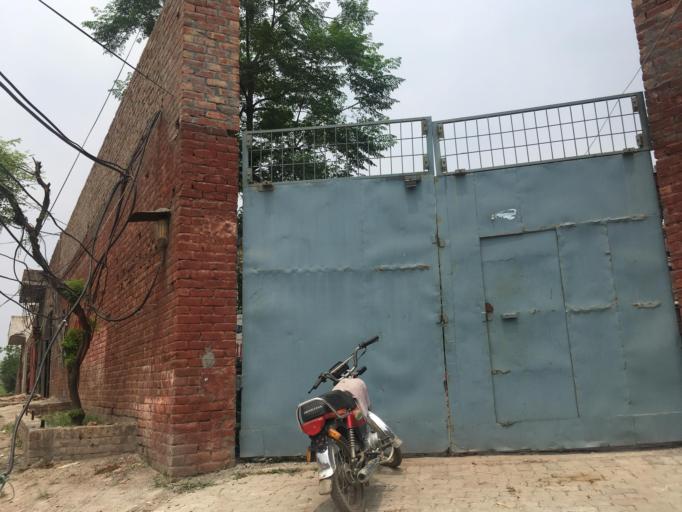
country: PK
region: Punjab
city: Lahore
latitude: 31.6126
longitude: 74.3521
